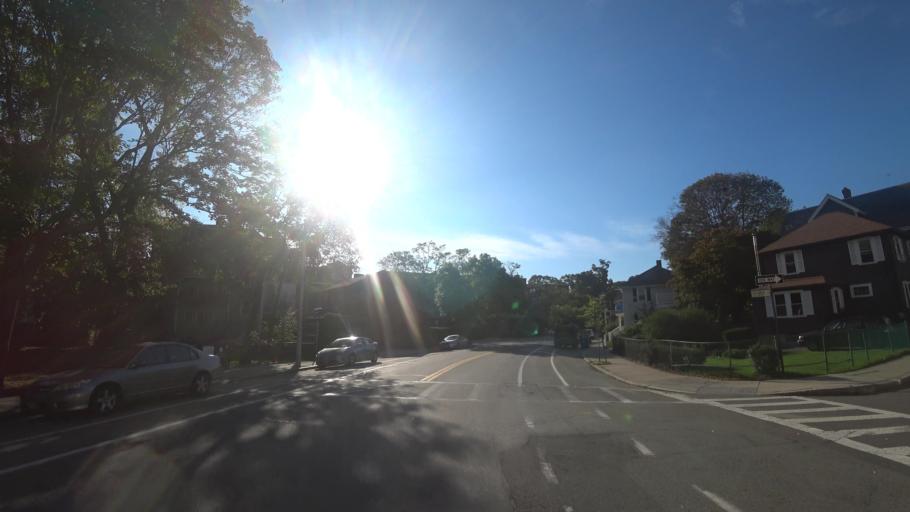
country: US
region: Massachusetts
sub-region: Norfolk County
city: Brookline
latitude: 42.3254
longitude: -71.1220
